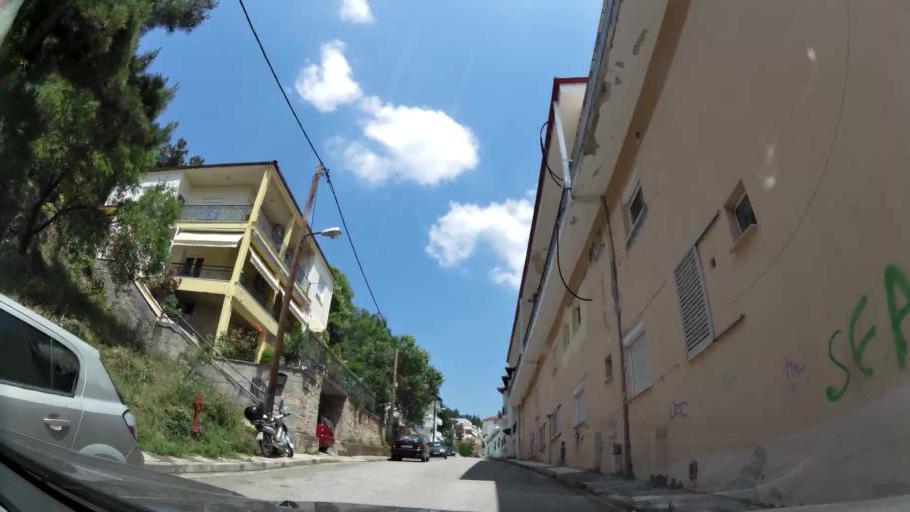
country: GR
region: West Macedonia
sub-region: Nomos Kozanis
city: Kozani
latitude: 40.3051
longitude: 21.7832
